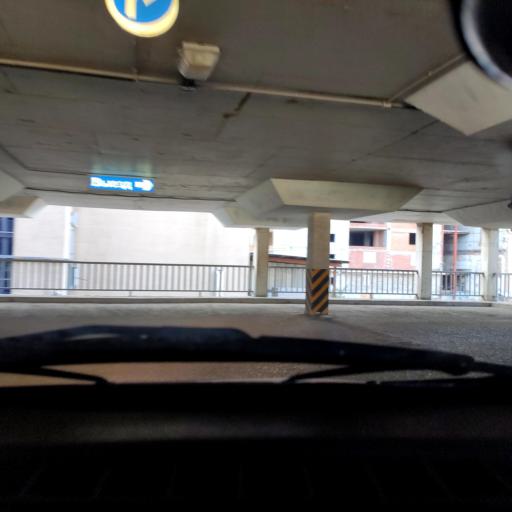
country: RU
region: Bashkortostan
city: Ufa
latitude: 54.7143
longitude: 55.9923
